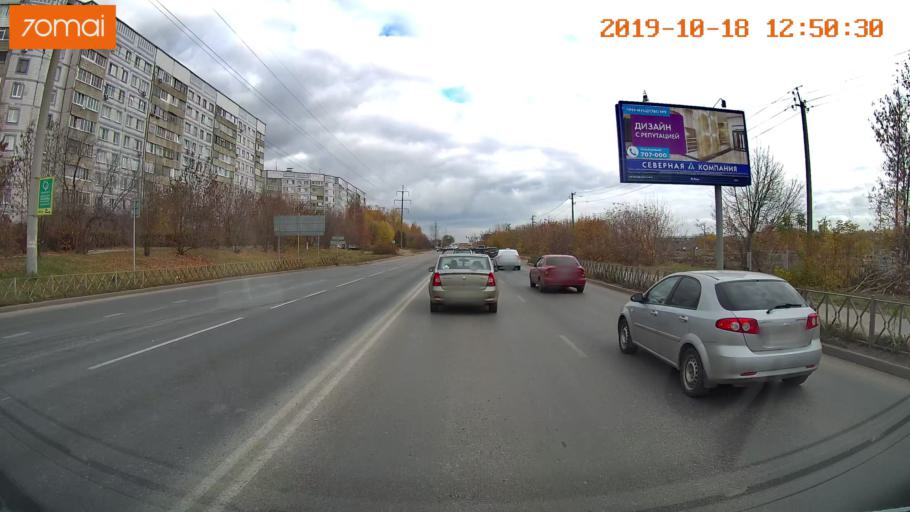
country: RU
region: Rjazan
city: Ryazan'
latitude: 54.6603
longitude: 39.6691
